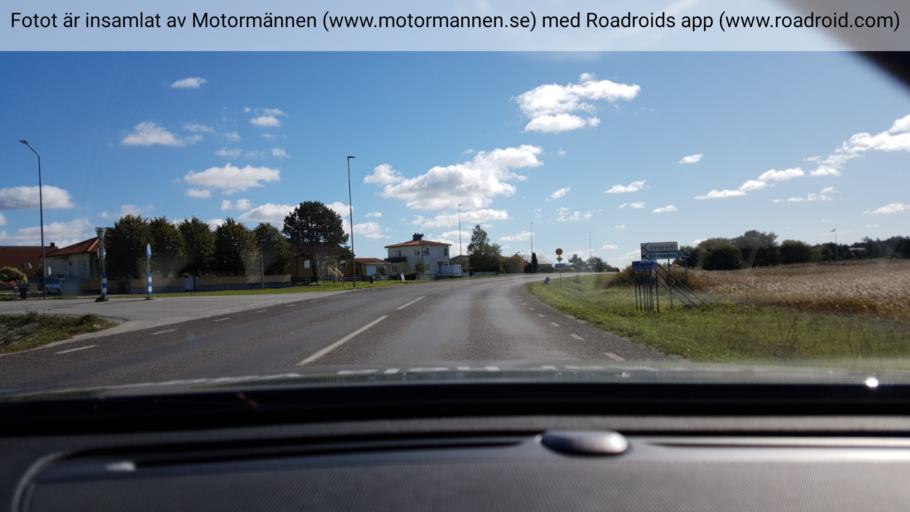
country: SE
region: Gotland
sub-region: Gotland
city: Slite
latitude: 57.6971
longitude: 18.7971
